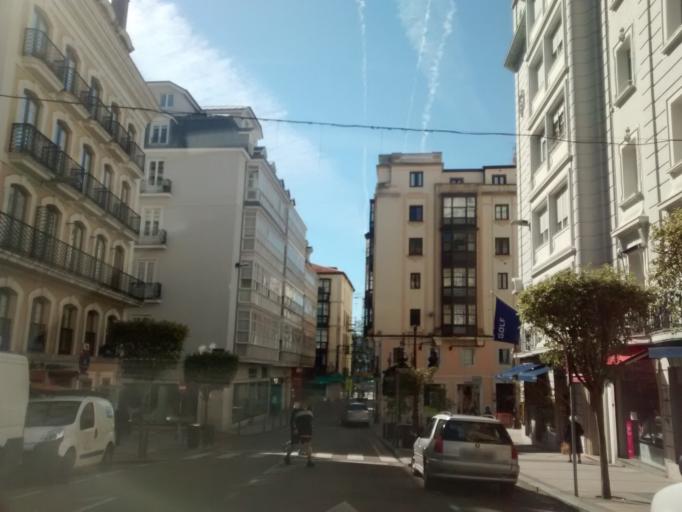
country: ES
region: Cantabria
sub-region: Provincia de Cantabria
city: Santander
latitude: 43.4628
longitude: -3.8053
